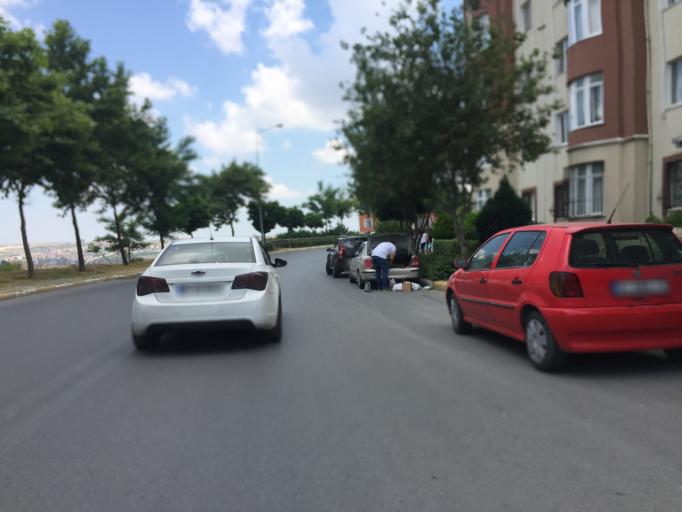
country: TR
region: Istanbul
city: Esenyurt
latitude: 41.0749
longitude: 28.6610
